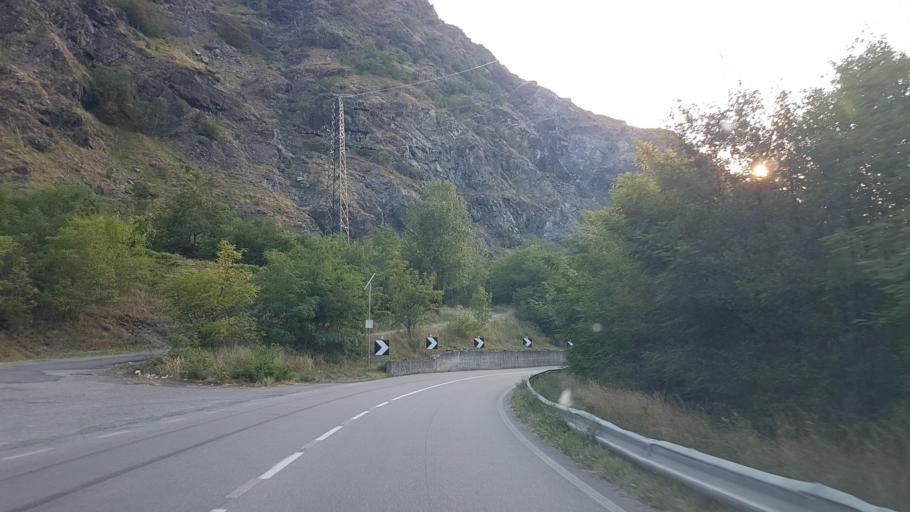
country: IT
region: Emilia-Romagna
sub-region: Provincia di Parma
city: Stazione Valmozzola
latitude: 44.5363
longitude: 9.8862
